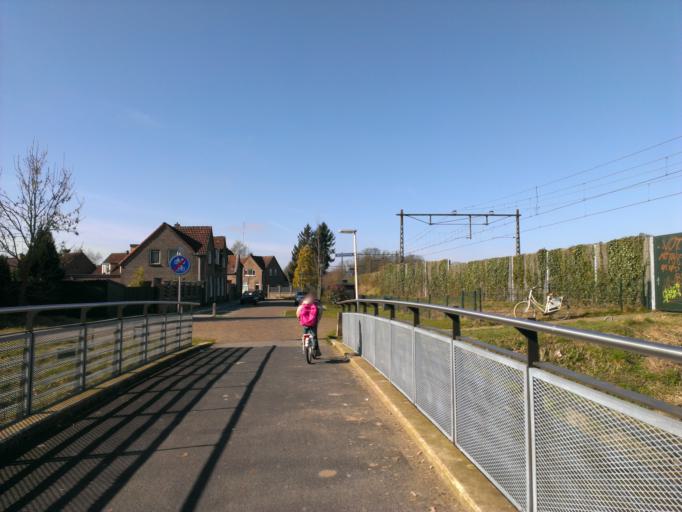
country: NL
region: Overijssel
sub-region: Gemeente Almelo
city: Almelo
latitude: 52.3403
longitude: 6.6695
